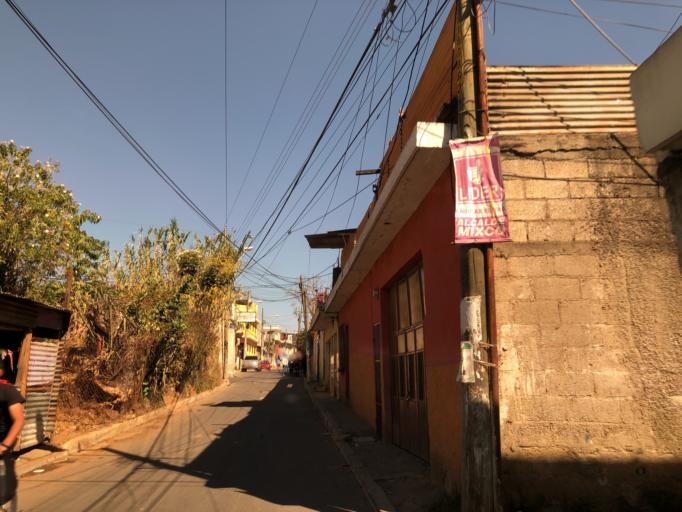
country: GT
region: Guatemala
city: Mixco
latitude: 14.6112
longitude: -90.5783
